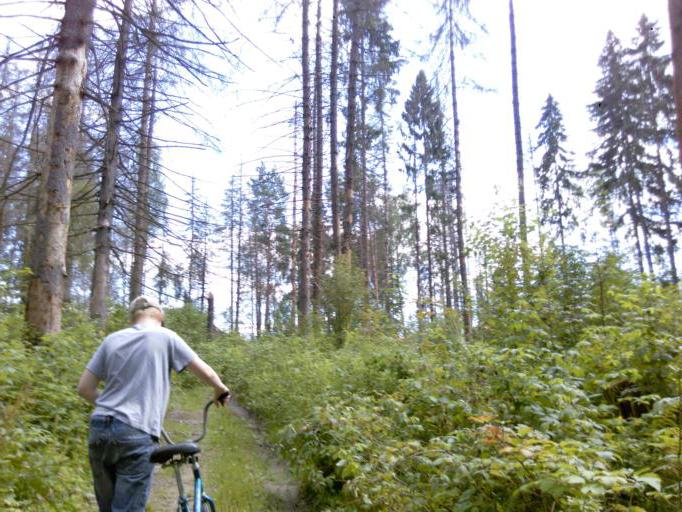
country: RU
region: Moskovskaya
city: Solnechnogorsk
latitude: 56.1356
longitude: 36.9092
